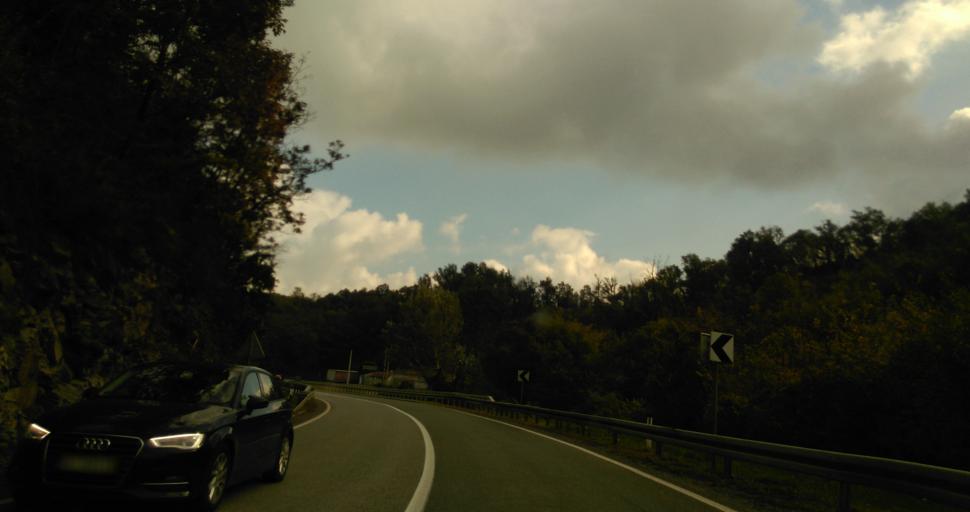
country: RS
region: Central Serbia
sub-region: Kolubarski Okrug
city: Ljig
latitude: 44.1899
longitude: 20.3168
